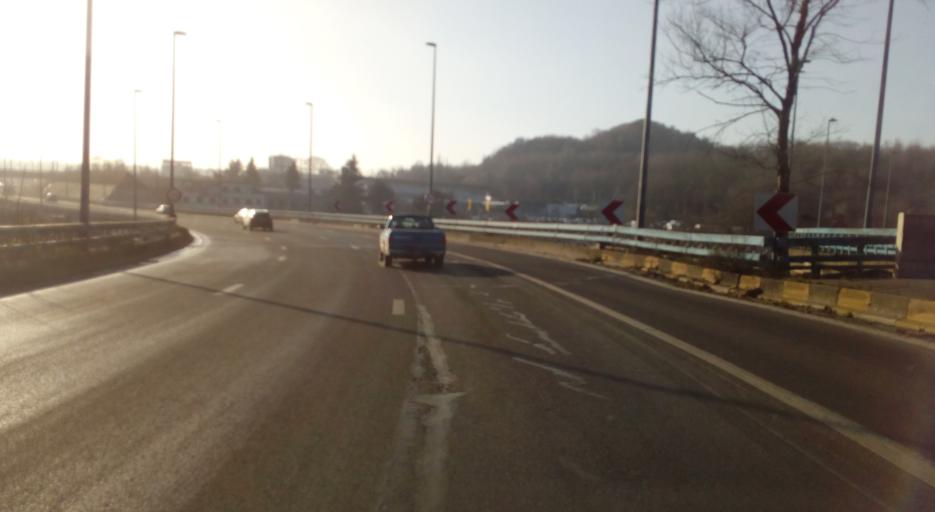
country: BE
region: Wallonia
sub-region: Province du Hainaut
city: Charleroi
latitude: 50.4183
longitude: 4.4411
